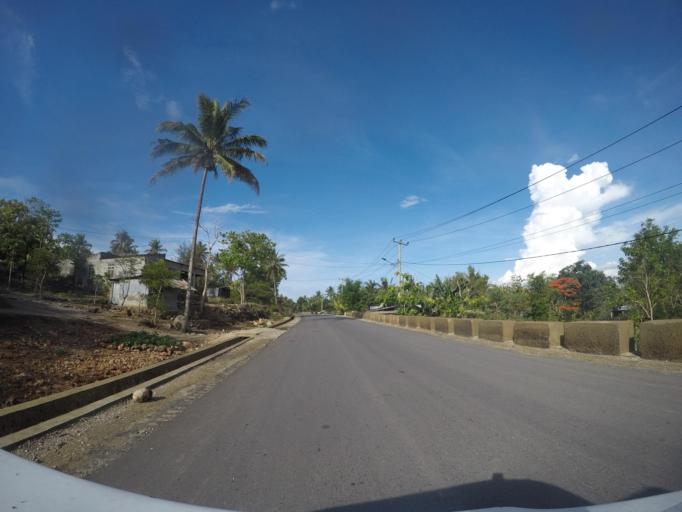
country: TL
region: Baucau
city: Baucau
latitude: -8.4915
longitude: 126.4569
